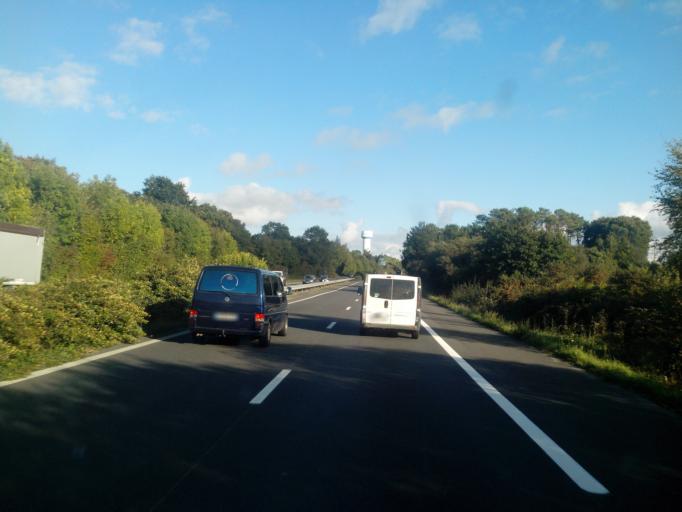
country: FR
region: Pays de la Loire
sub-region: Departement de la Loire-Atlantique
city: Missillac
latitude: 47.4813
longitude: -2.1894
